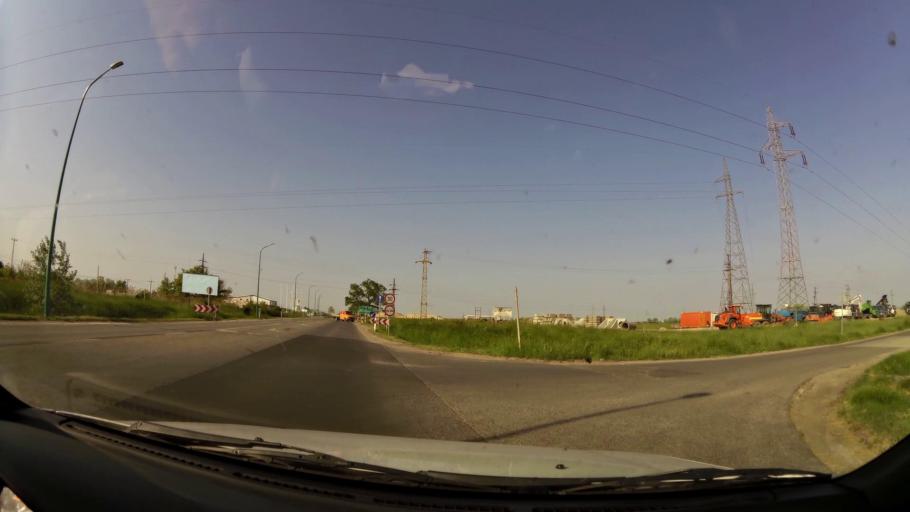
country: HU
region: Pest
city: Cegled
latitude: 47.1925
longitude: 19.8104
